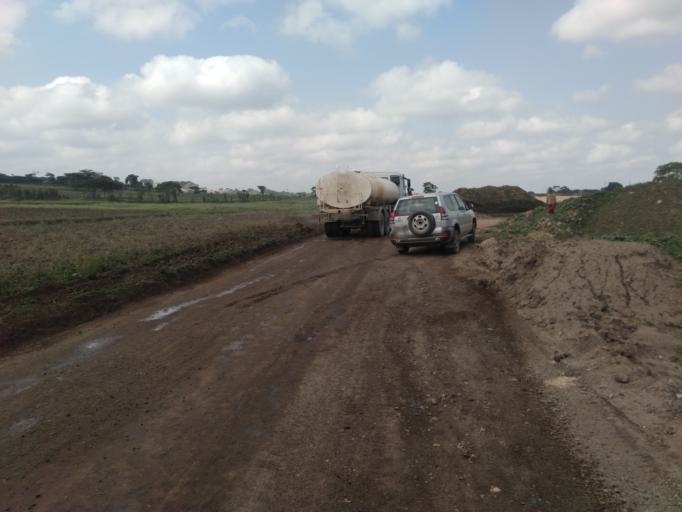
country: ET
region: Oromiya
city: Shashemene
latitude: 7.3999
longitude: 38.6599
